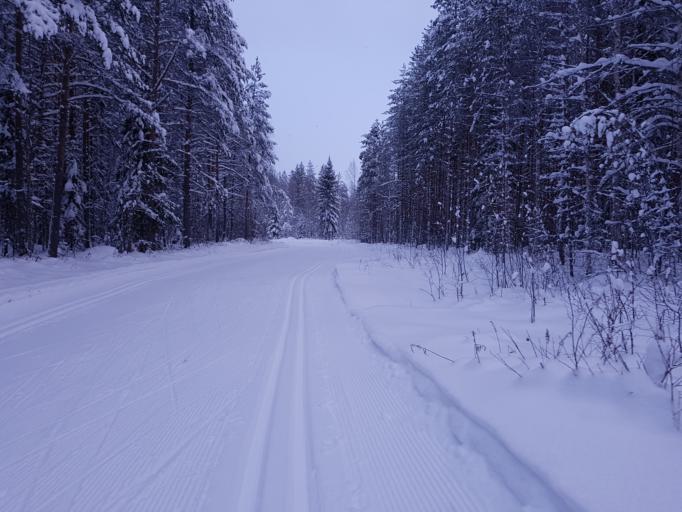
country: FI
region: Kainuu
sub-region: Kehys-Kainuu
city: Kuhmo
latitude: 64.1134
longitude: 29.5658
